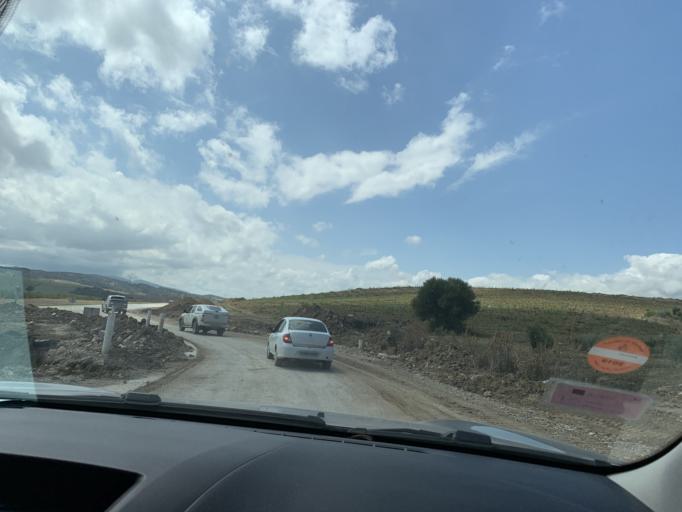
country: TN
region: Silyanah
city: Bu `Aradah
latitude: 36.1986
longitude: 9.7085
